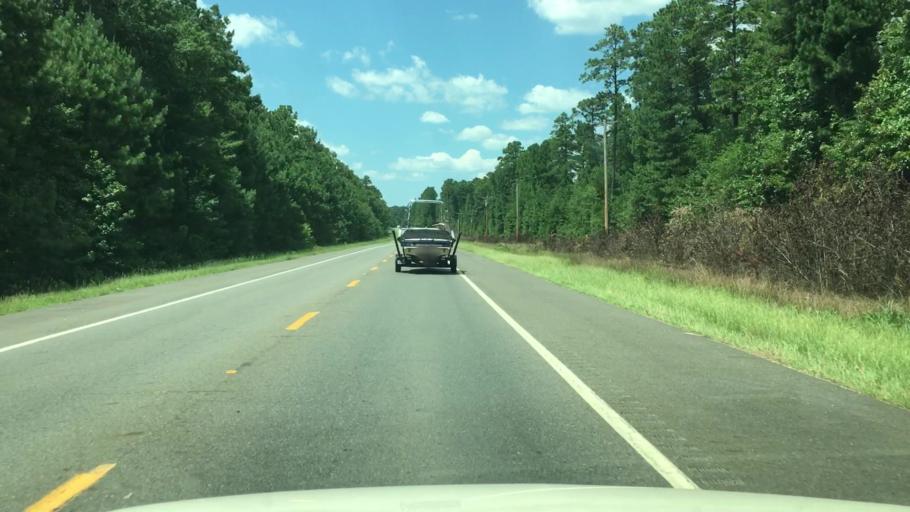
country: US
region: Arkansas
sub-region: Clark County
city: Arkadelphia
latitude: 34.1916
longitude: -93.0735
